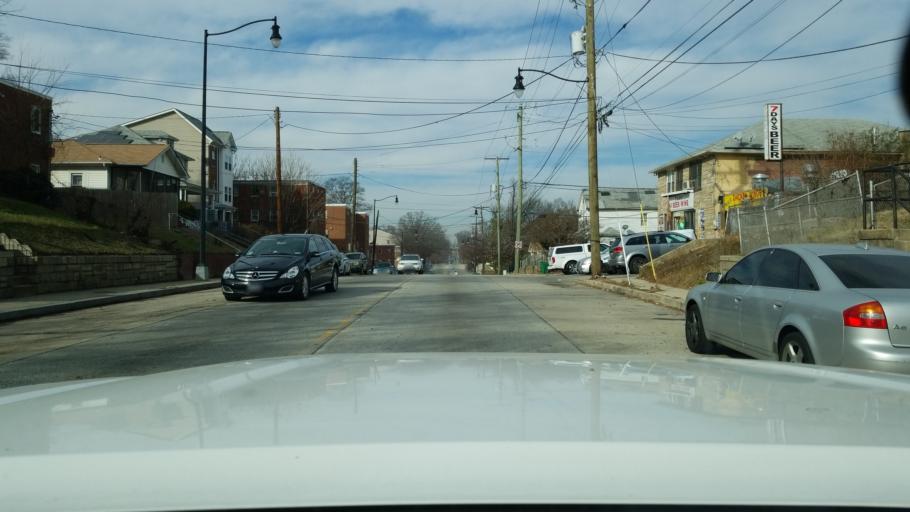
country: US
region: Maryland
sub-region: Prince George's County
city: Fairmount Heights
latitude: 38.8962
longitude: -76.9136
